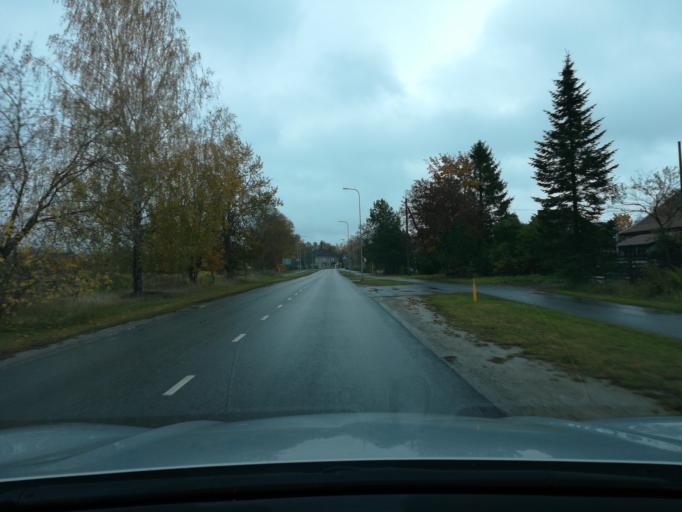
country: EE
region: Ida-Virumaa
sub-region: Johvi vald
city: Johvi
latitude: 59.3139
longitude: 27.4475
